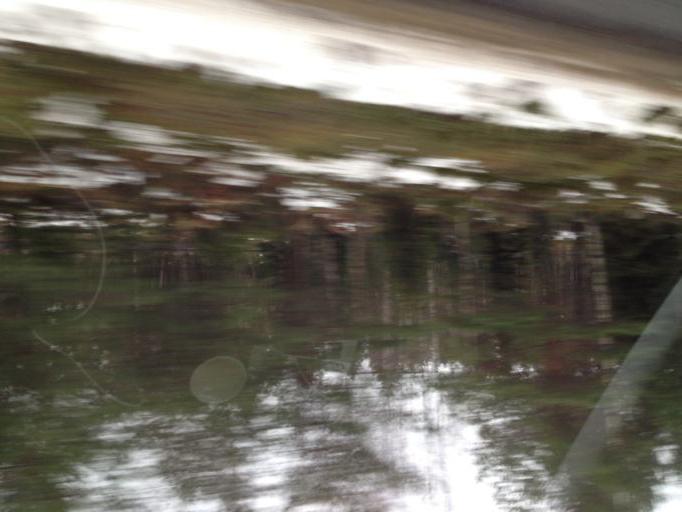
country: FI
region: Uusimaa
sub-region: Raaseporin
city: Ekenaes
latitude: 59.9373
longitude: 23.3346
